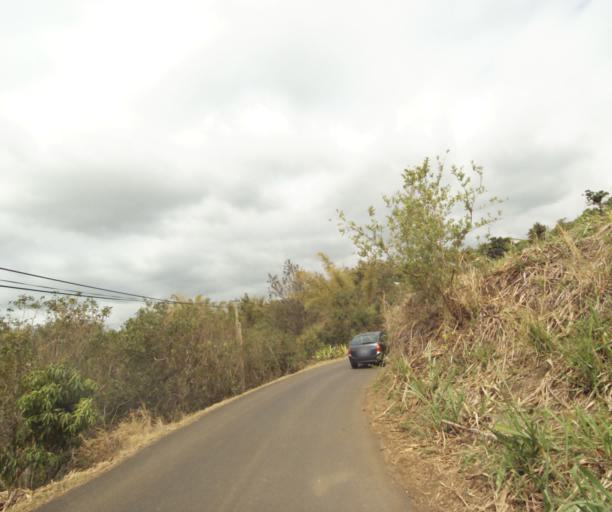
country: RE
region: Reunion
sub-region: Reunion
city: Saint-Paul
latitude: -21.0304
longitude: 55.2983
